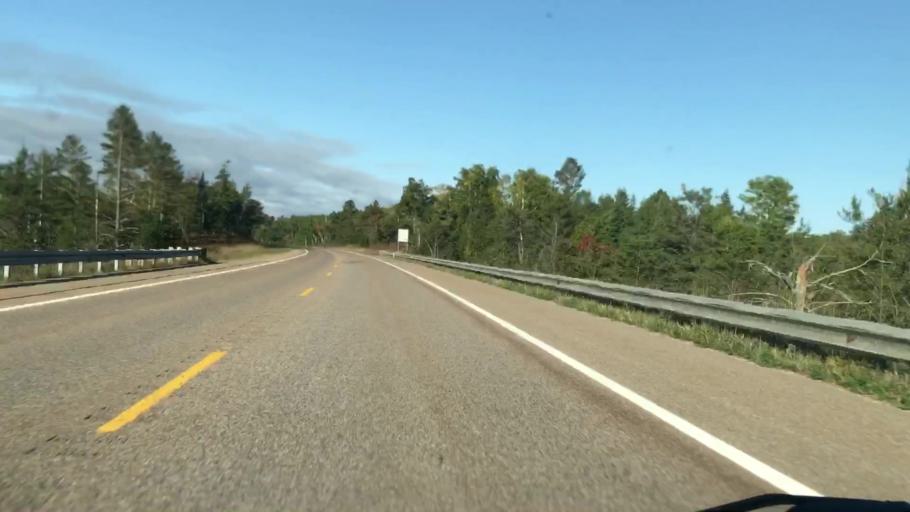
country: US
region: Michigan
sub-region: Mackinac County
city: Saint Ignace
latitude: 46.3580
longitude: -84.8873
